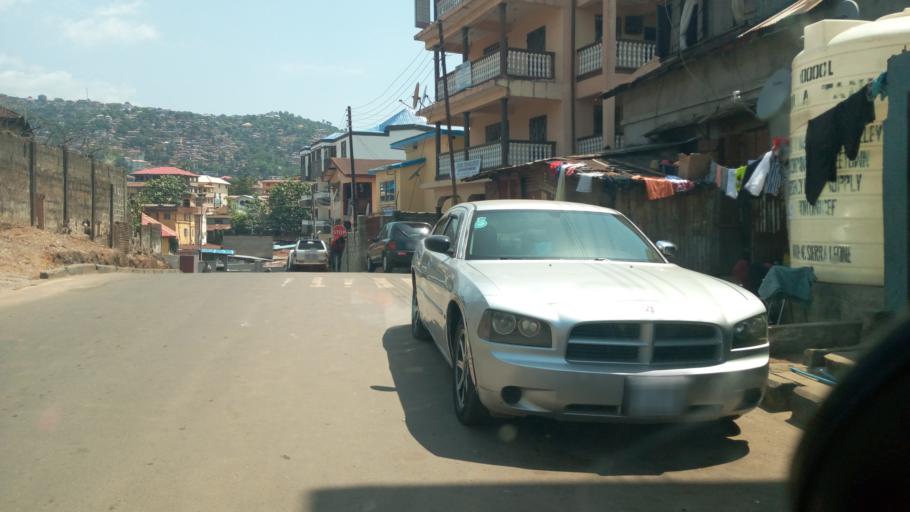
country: SL
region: Western Area
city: Freetown
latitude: 8.4793
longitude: -13.2442
